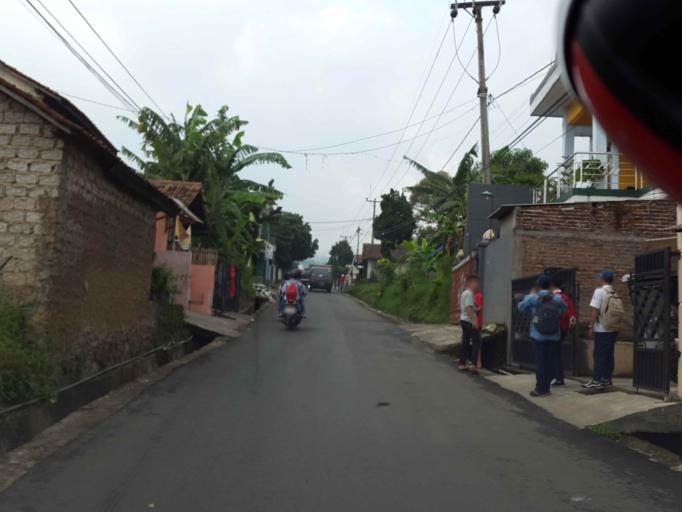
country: ID
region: West Java
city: Cimahi
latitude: -6.8444
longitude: 107.5718
